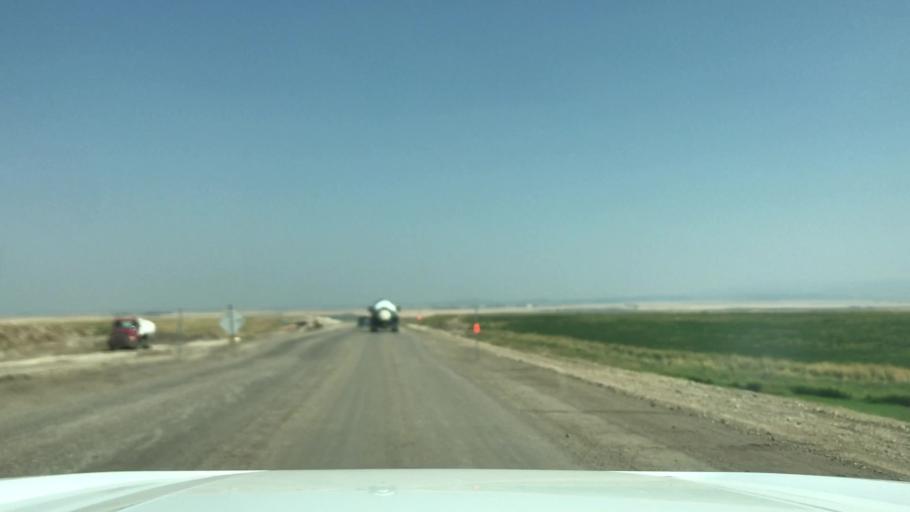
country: US
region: Montana
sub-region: Fergus County
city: Lewistown
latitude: 46.9988
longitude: -109.8165
